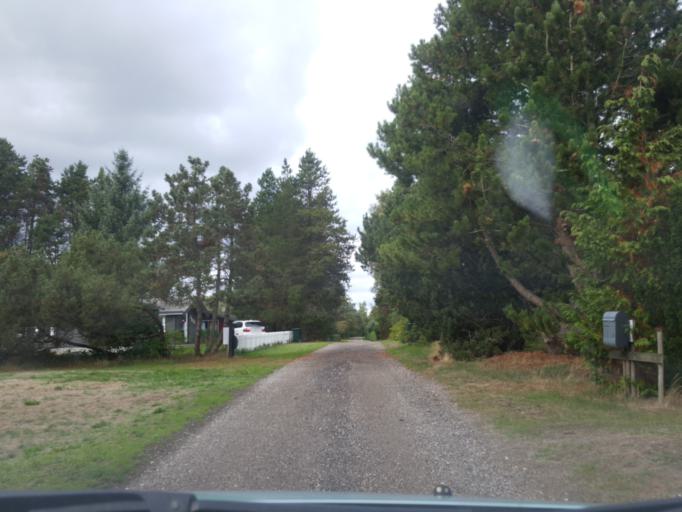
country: DK
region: Zealand
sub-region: Guldborgsund Kommune
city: Nykobing Falster
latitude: 54.6543
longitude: 11.9492
